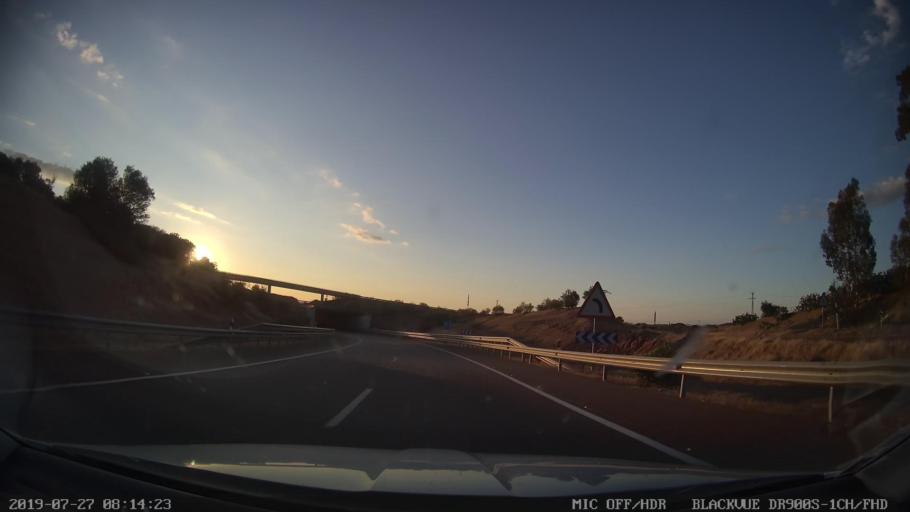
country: ES
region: Extremadura
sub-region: Provincia de Badajoz
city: Calamonte
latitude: 38.9097
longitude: -6.3769
